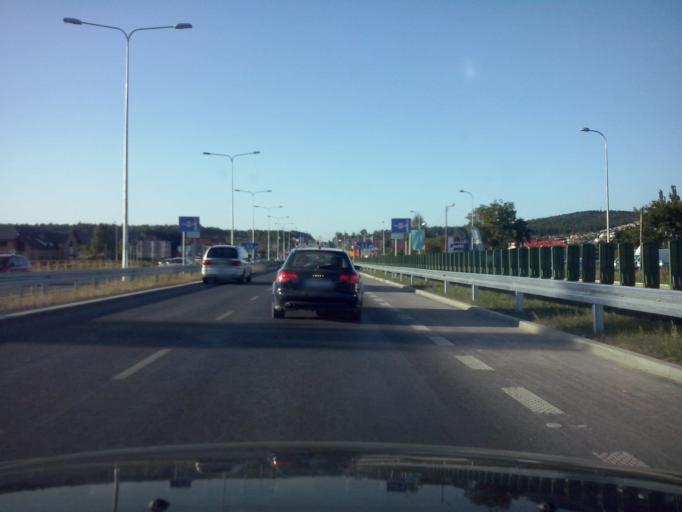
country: PL
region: Swietokrzyskie
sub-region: Powiat kielecki
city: Kielce
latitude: 50.8209
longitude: 20.6222
